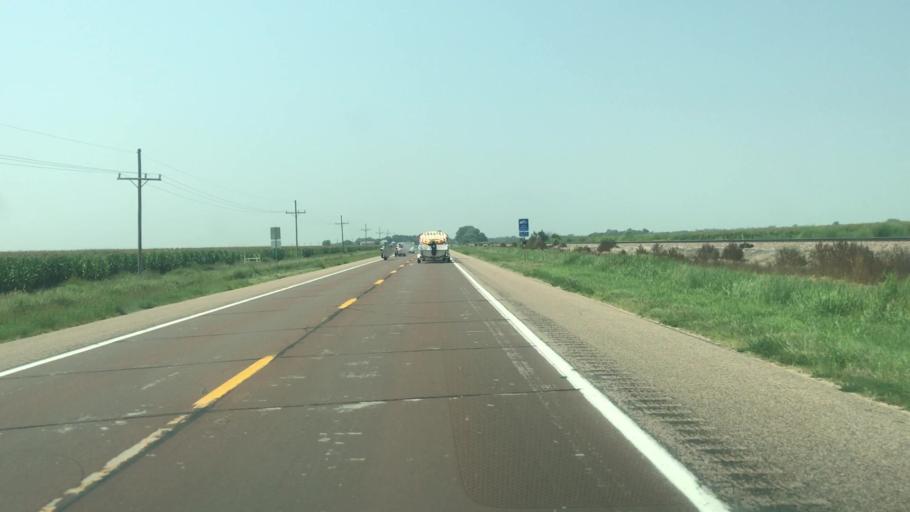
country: US
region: Nebraska
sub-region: Hall County
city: Grand Island
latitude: 40.9656
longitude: -98.4390
